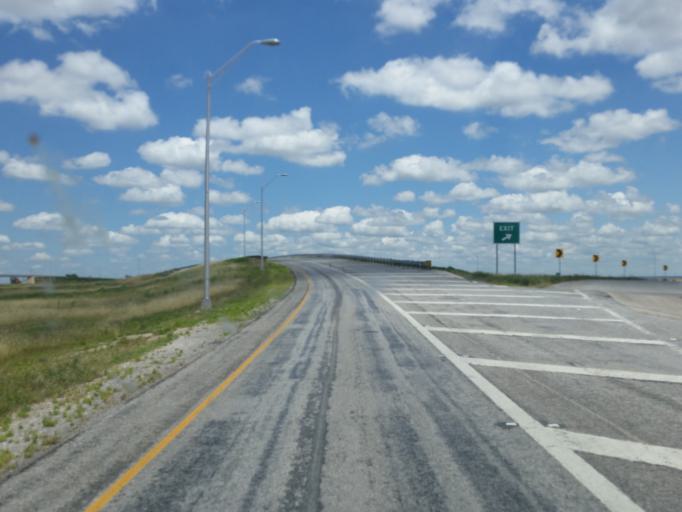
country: US
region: Texas
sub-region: Nolan County
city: Roscoe
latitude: 32.4460
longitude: -100.5095
